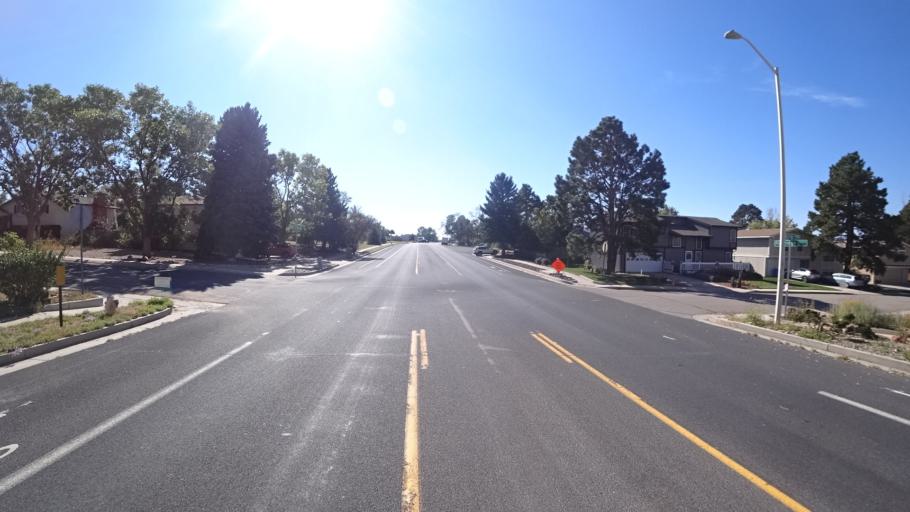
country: US
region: Colorado
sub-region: El Paso County
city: Cimarron Hills
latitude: 38.9186
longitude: -104.7654
